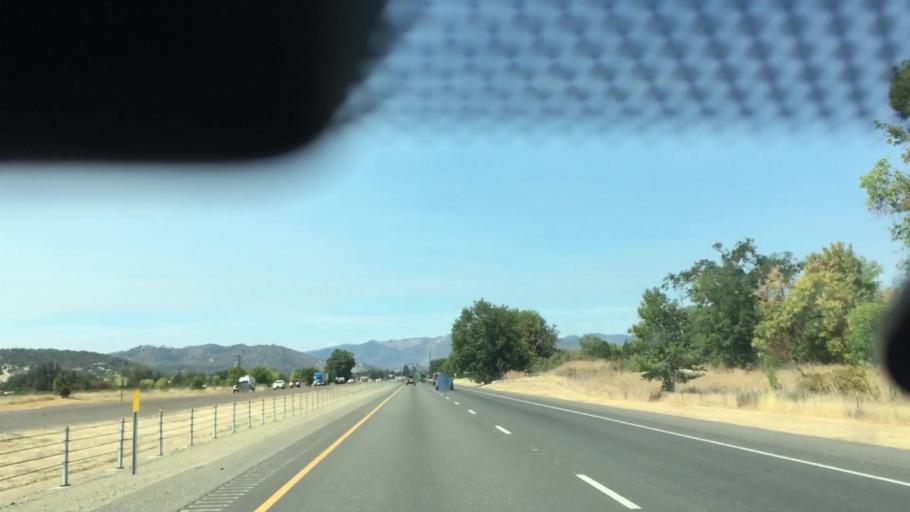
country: US
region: Oregon
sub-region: Jackson County
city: Central Point
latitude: 42.3972
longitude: -122.9291
